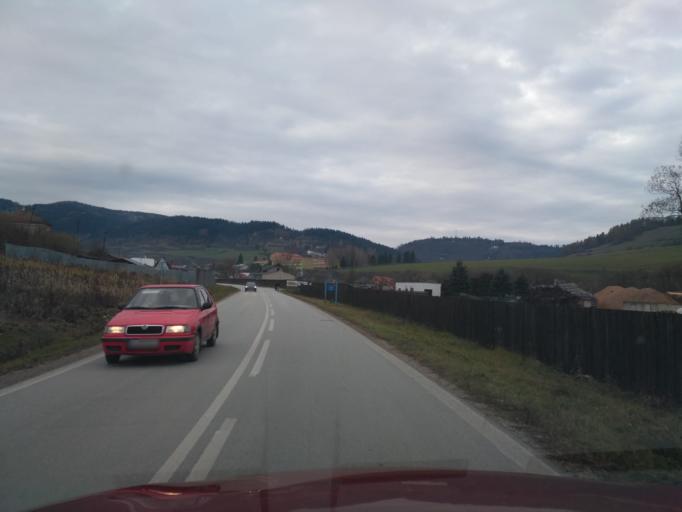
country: SK
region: Kosicky
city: Spisska Nova Ves
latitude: 48.8388
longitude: 20.6329
